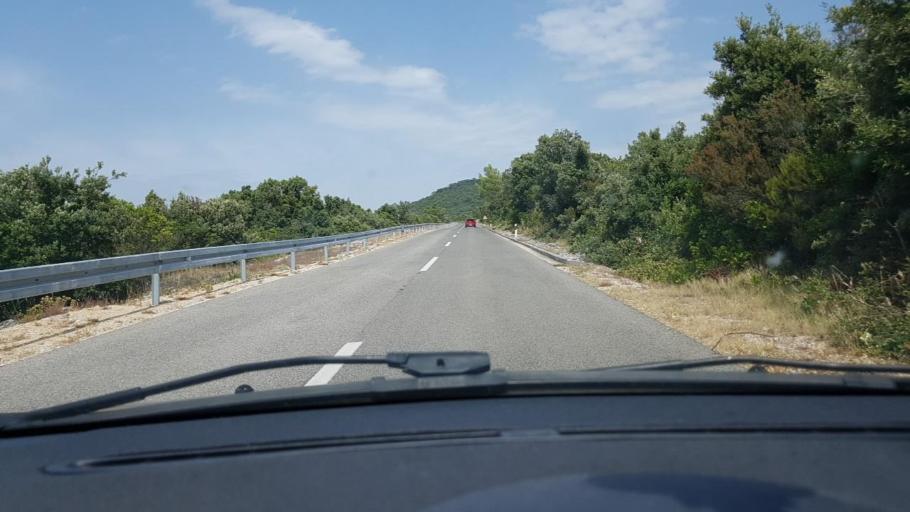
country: HR
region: Dubrovacko-Neretvanska
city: Smokvica
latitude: 42.9481
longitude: 16.9675
